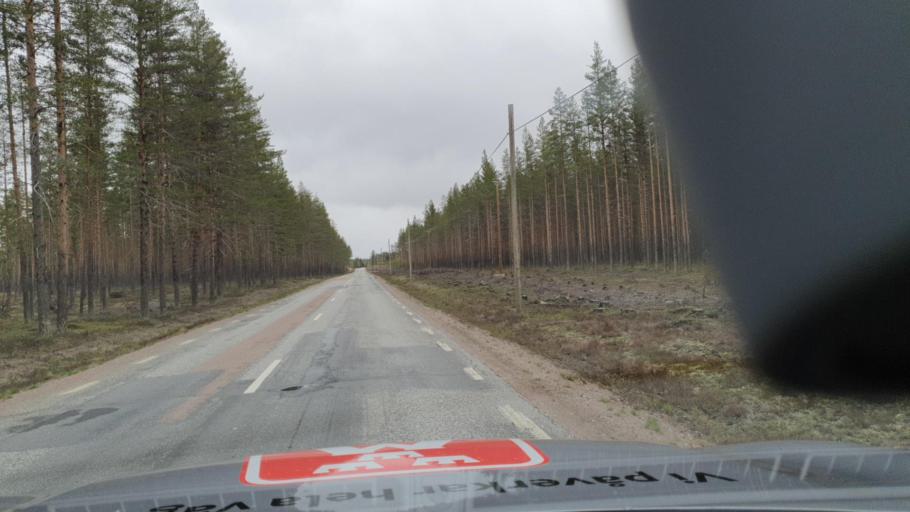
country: SE
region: Vaesternorrland
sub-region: Solleftea Kommun
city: Solleftea
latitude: 63.6019
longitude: 17.5397
